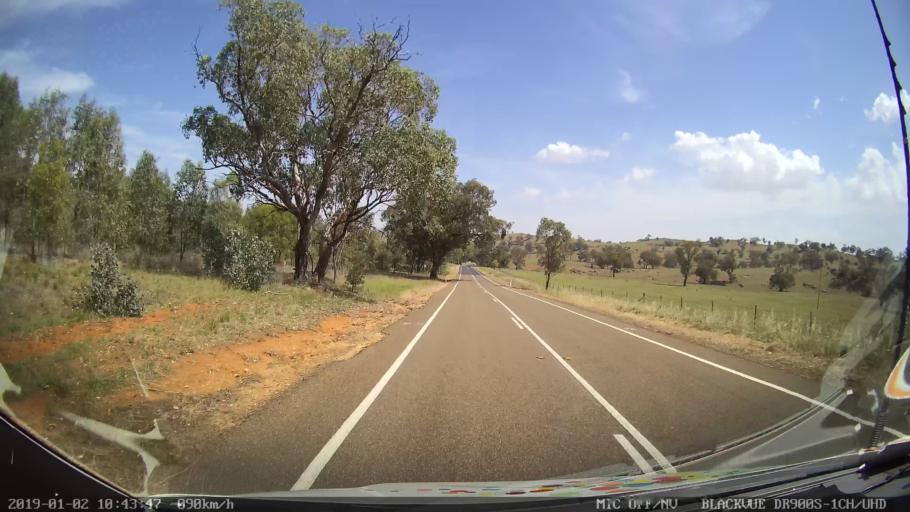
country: AU
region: New South Wales
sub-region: Cootamundra
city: Cootamundra
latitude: -34.7681
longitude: 148.3016
